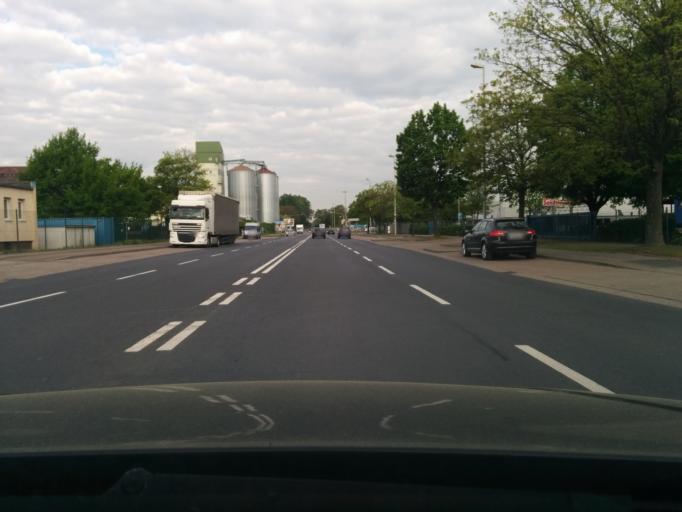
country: DE
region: Lower Saxony
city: Vordorf
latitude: 52.3155
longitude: 10.4916
